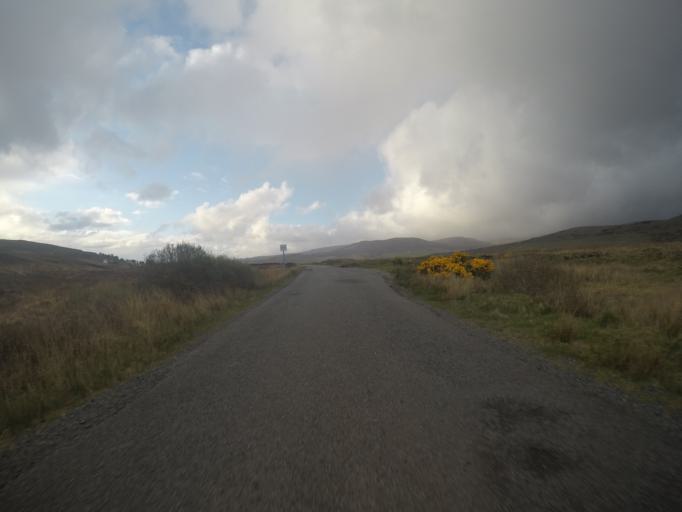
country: GB
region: Scotland
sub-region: Highland
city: Isle of Skye
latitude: 57.4610
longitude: -6.2965
